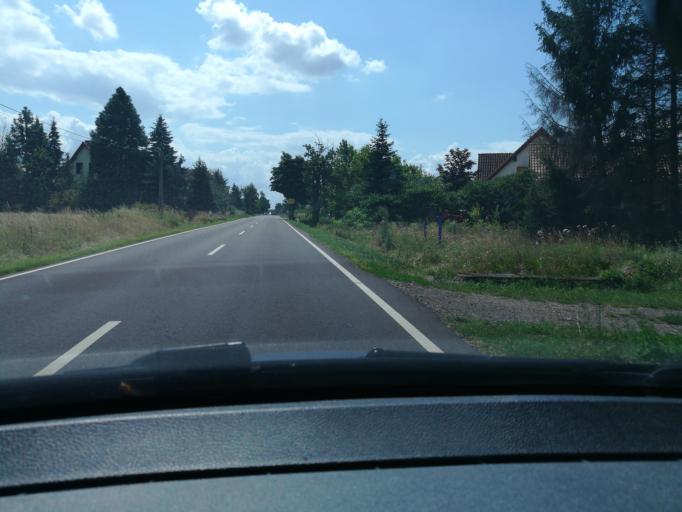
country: DE
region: Saxony-Anhalt
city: Rogatz
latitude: 52.3256
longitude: 11.7735
